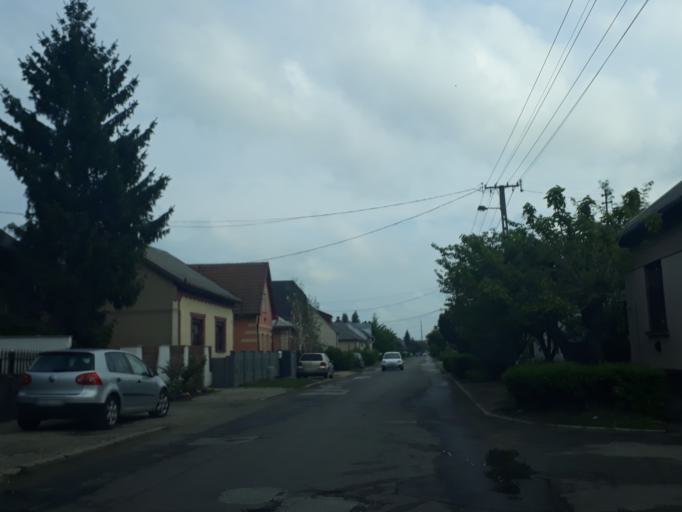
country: HU
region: Szabolcs-Szatmar-Bereg
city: Kisvarda
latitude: 48.2183
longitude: 22.0749
